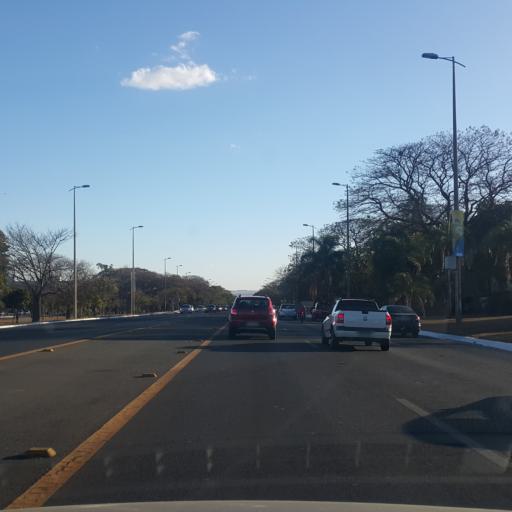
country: BR
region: Federal District
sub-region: Brasilia
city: Brasilia
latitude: -15.8192
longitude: -47.9038
